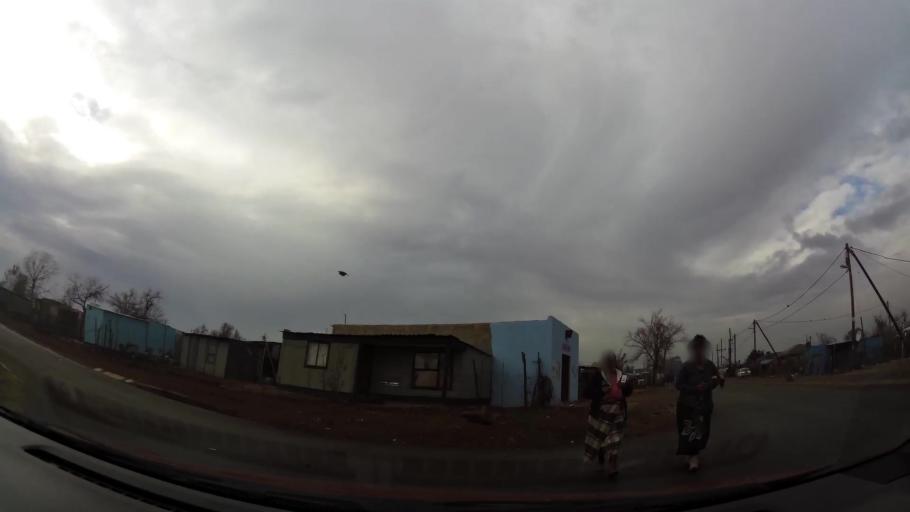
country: ZA
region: Gauteng
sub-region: City of Johannesburg Metropolitan Municipality
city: Soweto
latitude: -26.2841
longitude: 27.8374
